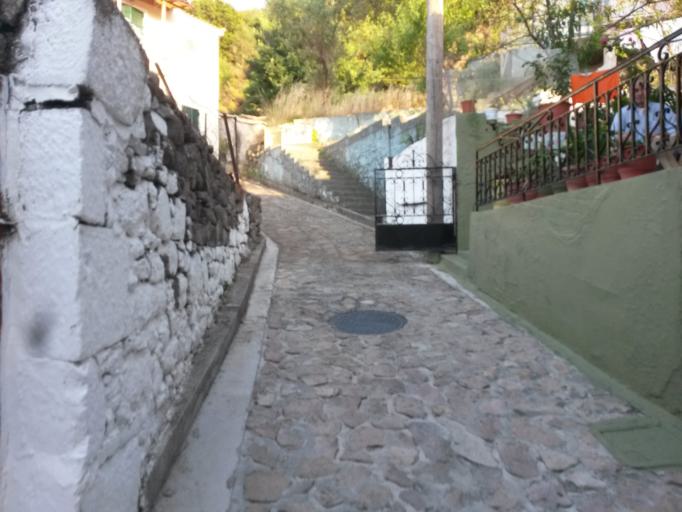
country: GR
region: North Aegean
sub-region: Nomos Lesvou
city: Mantamados
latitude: 39.3733
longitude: 26.3034
